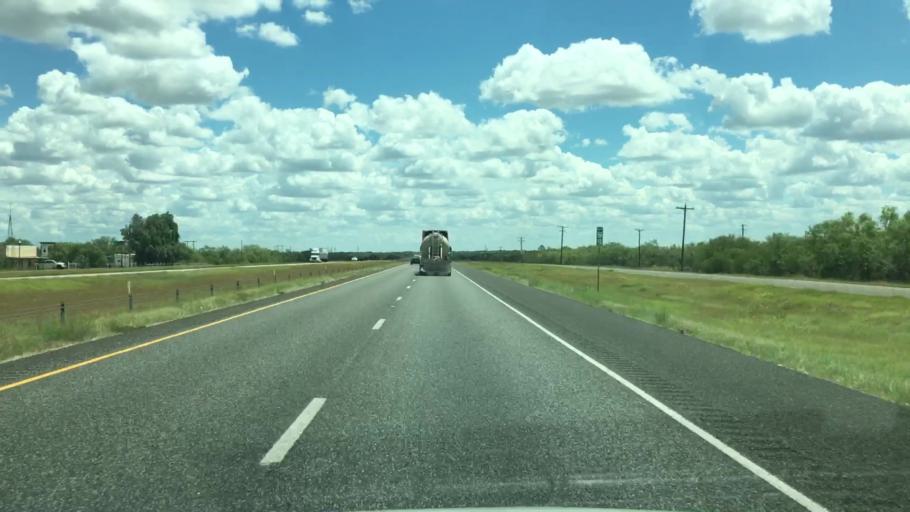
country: US
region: Texas
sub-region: Atascosa County
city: Pleasanton
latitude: 28.8540
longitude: -98.3836
